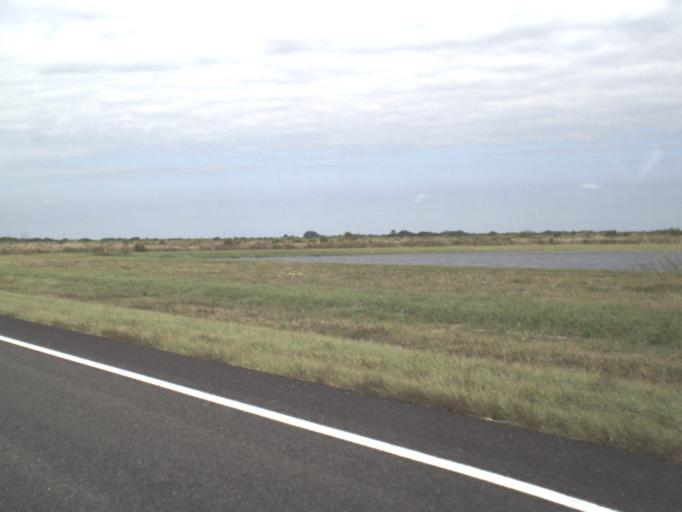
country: US
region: Florida
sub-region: Glades County
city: Moore Haven
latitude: 26.7532
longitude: -81.1180
